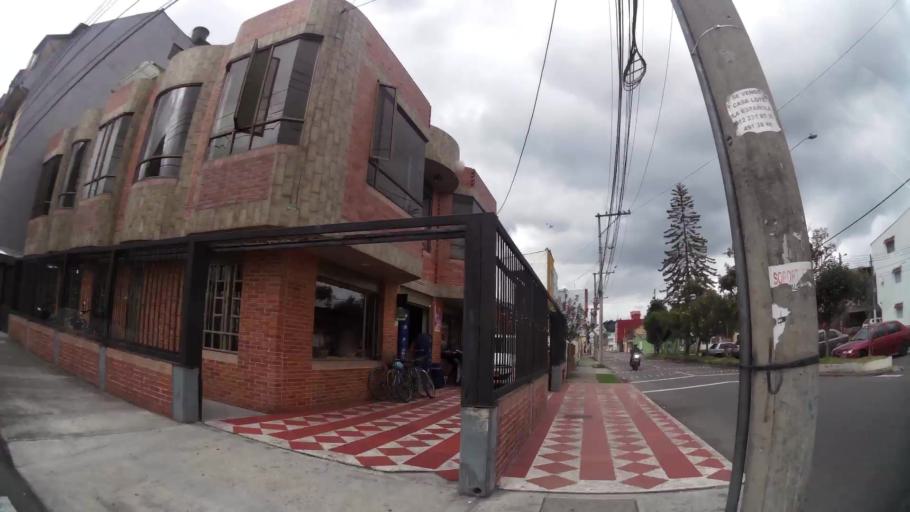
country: CO
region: Bogota D.C.
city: Barrio San Luis
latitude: 4.7023
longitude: -74.0985
